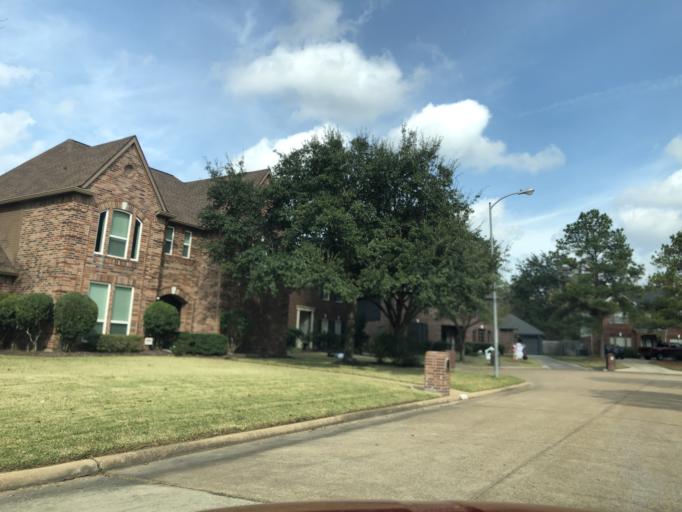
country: US
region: Texas
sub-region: Harris County
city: Tomball
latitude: 30.0342
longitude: -95.5416
